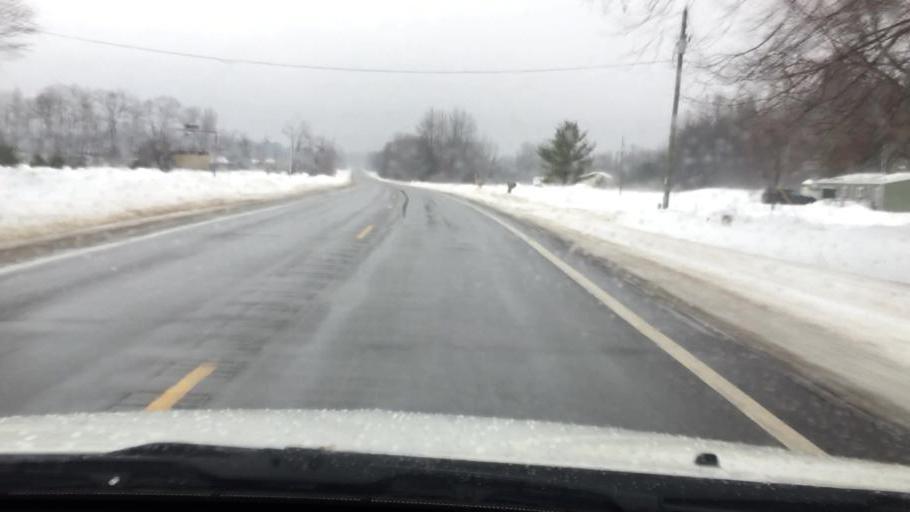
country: US
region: Michigan
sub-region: Charlevoix County
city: East Jordan
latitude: 45.0658
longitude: -85.0829
